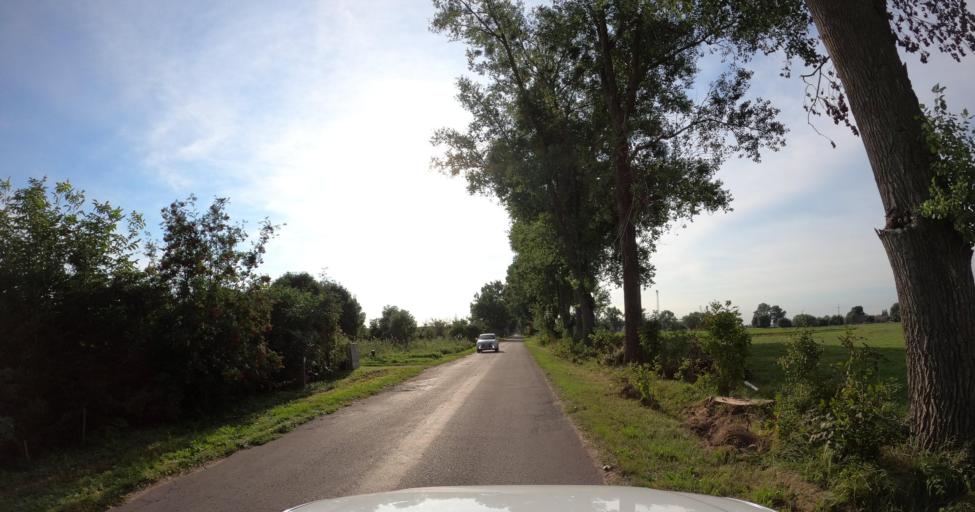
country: PL
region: West Pomeranian Voivodeship
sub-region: Powiat goleniowski
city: Goleniow
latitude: 53.5169
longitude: 14.7236
